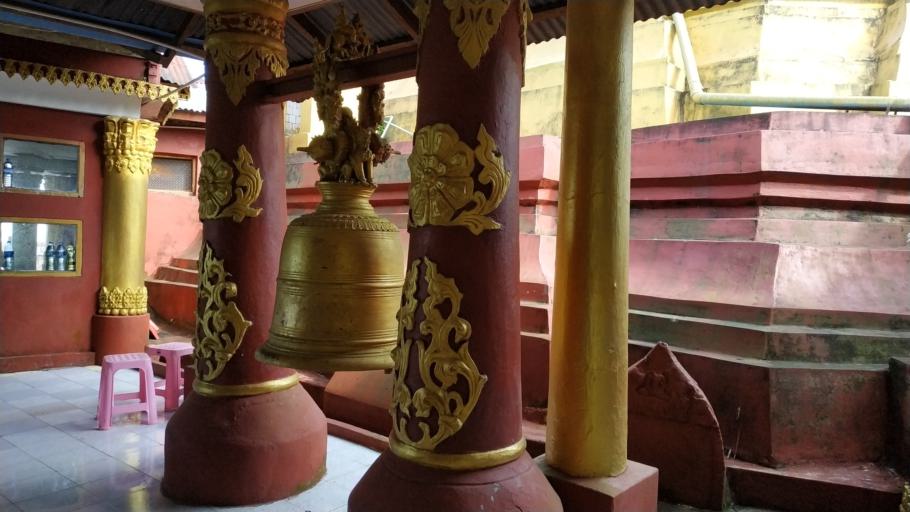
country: MM
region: Mon
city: Thaton
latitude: 16.9253
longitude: 97.3819
